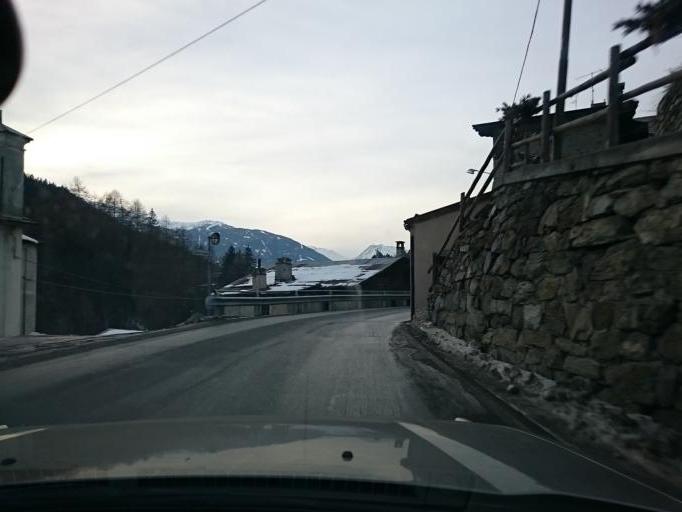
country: IT
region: Lombardy
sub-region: Provincia di Sondrio
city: San Nicolo
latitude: 46.4628
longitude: 10.4080
